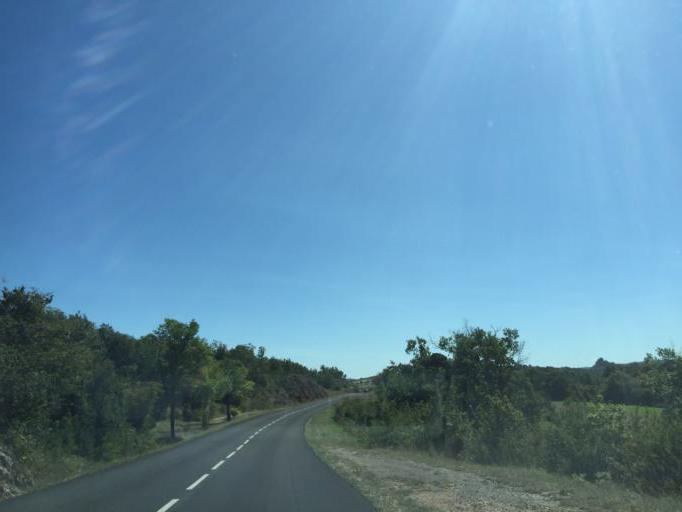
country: FR
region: Languedoc-Roussillon
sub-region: Departement de l'Herault
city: Lodeve
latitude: 43.8916
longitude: 3.3107
